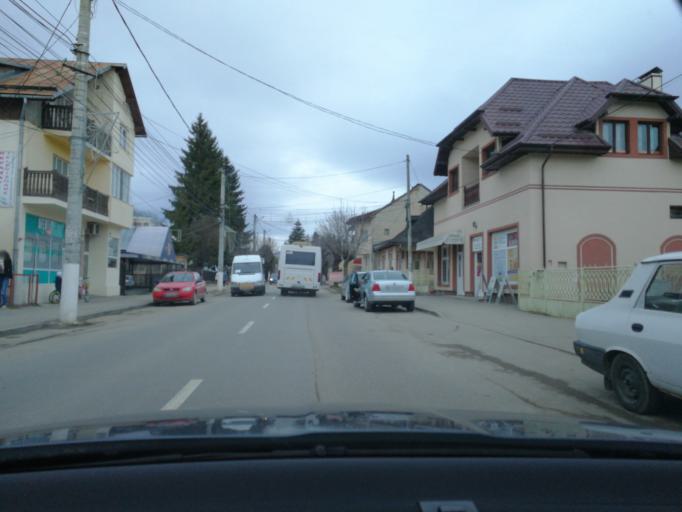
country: RO
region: Prahova
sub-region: Oras Breaza
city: Breaza
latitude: 45.1774
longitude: 25.6704
